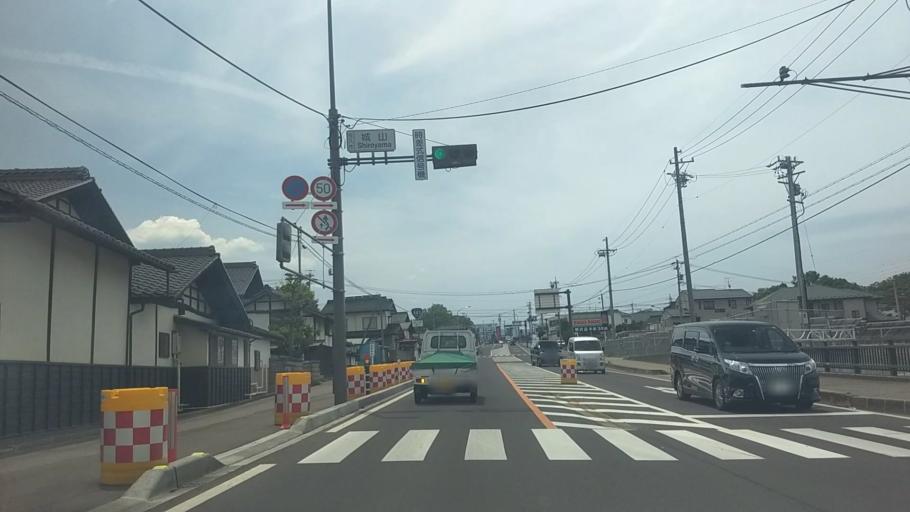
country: JP
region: Nagano
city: Saku
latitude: 36.1916
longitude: 138.4799
